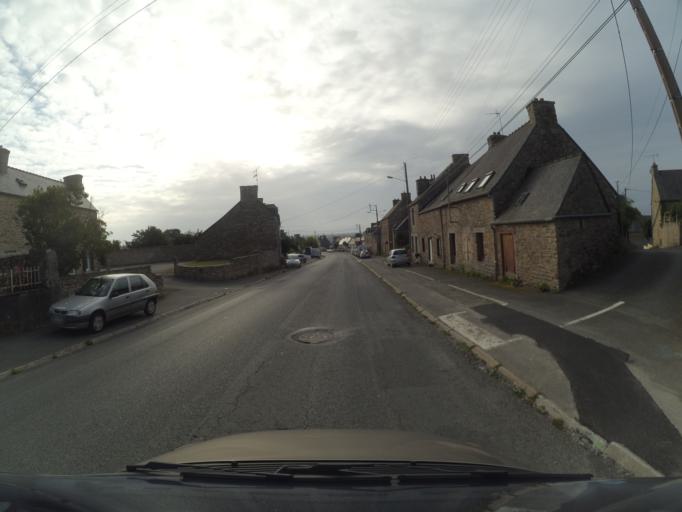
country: FR
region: Brittany
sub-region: Departement des Cotes-d'Armor
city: Graces
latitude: 48.5661
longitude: -3.1762
